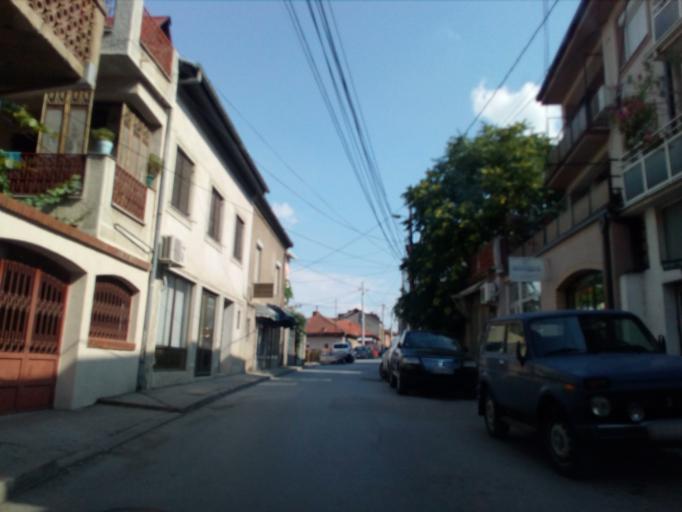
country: MK
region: Veles
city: Veles
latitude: 41.7162
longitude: 21.7825
